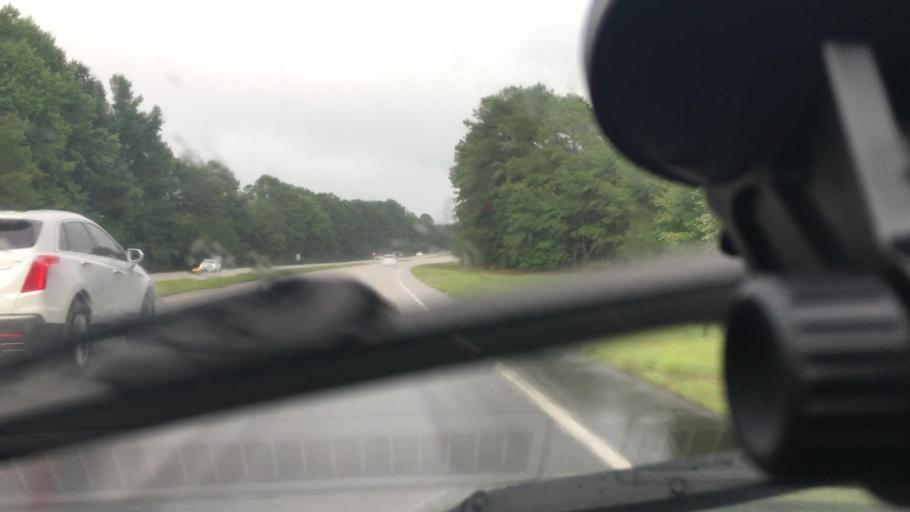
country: US
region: North Carolina
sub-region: Wilson County
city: Wilson
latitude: 35.7646
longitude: -78.0186
